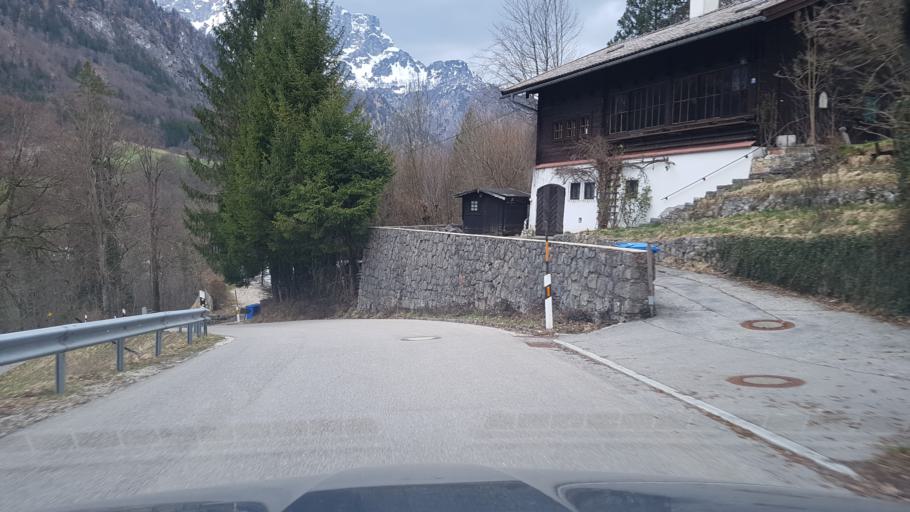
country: DE
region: Bavaria
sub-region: Upper Bavaria
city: Marktschellenberg
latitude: 47.6883
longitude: 13.0502
